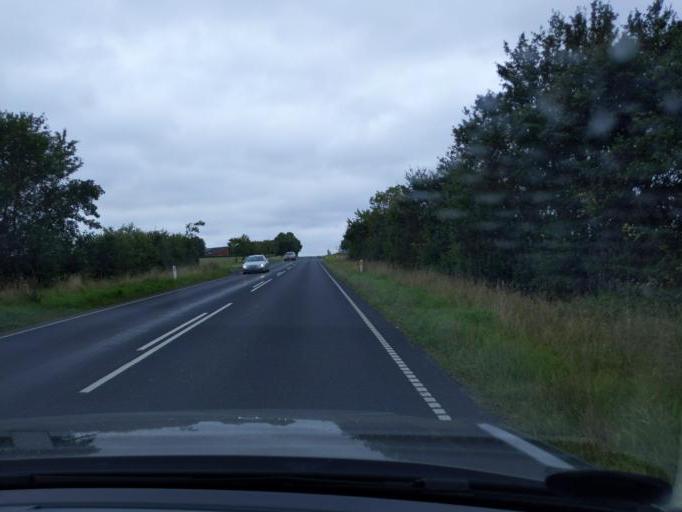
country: DK
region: Central Jutland
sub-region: Randers Kommune
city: Spentrup
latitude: 56.5209
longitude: 9.9365
